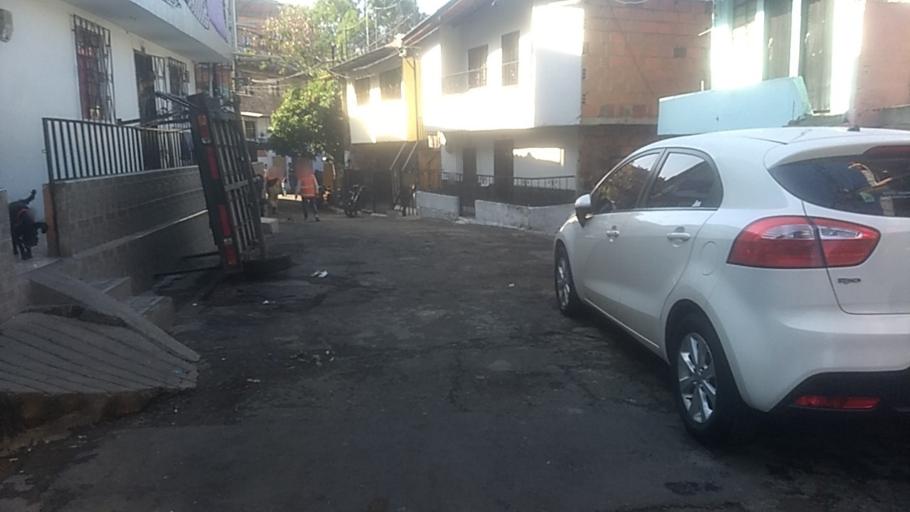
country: CO
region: Antioquia
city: Bello
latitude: 6.2982
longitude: -75.5477
